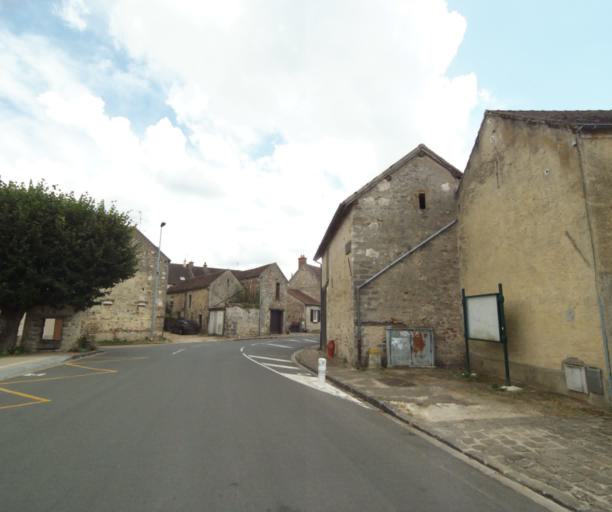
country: FR
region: Ile-de-France
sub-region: Departement de Seine-et-Marne
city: Hericy
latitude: 48.4470
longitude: 2.7744
